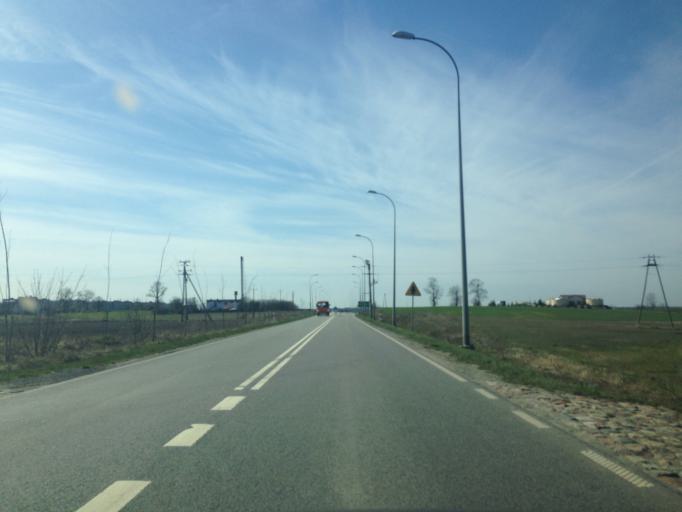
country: PL
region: Pomeranian Voivodeship
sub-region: Powiat starogardzki
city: Smetowo Graniczne
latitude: 53.7422
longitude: 18.6567
